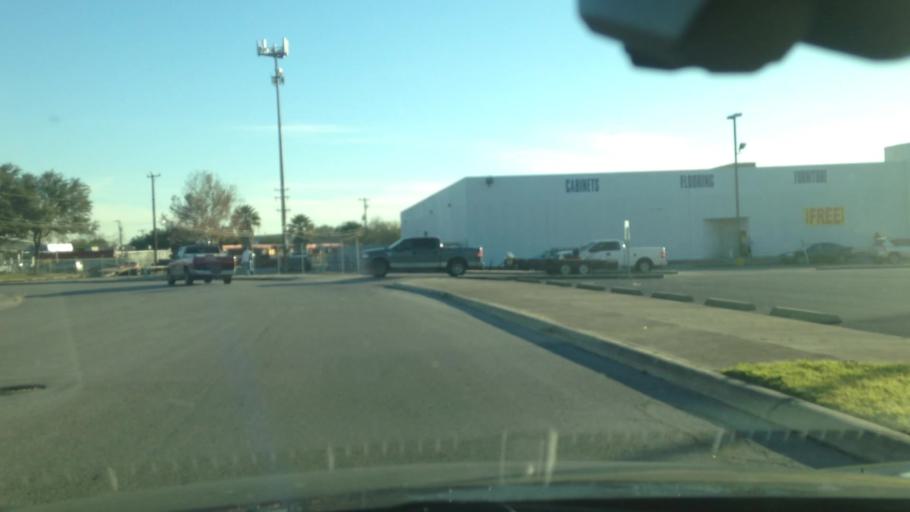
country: US
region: Texas
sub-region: Bexar County
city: Windcrest
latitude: 29.5098
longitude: -98.3817
